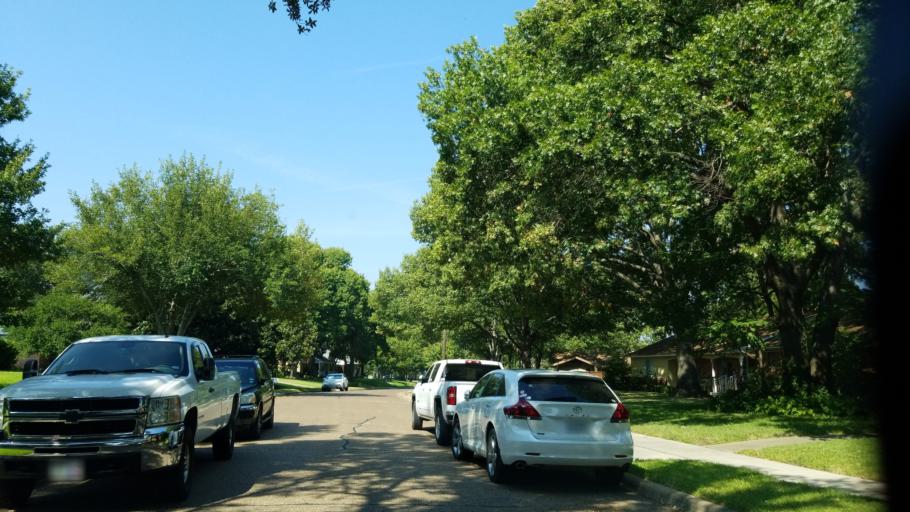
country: US
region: Texas
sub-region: Dallas County
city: Richardson
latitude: 32.9608
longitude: -96.7414
